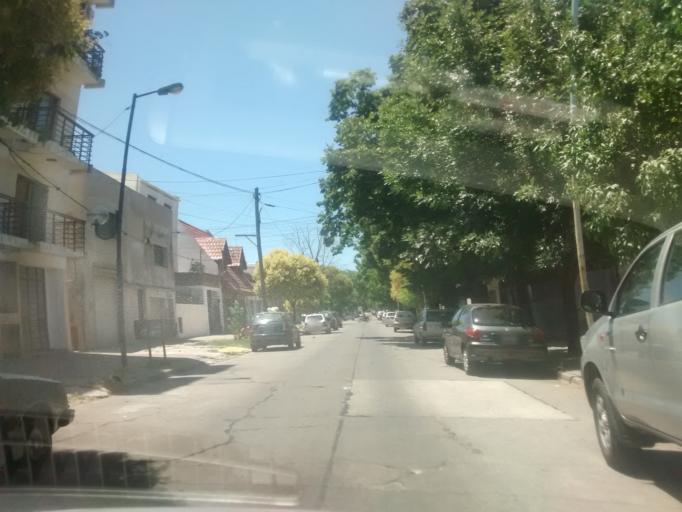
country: AR
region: Buenos Aires
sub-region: Partido de La Plata
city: La Plata
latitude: -34.9350
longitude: -57.9426
